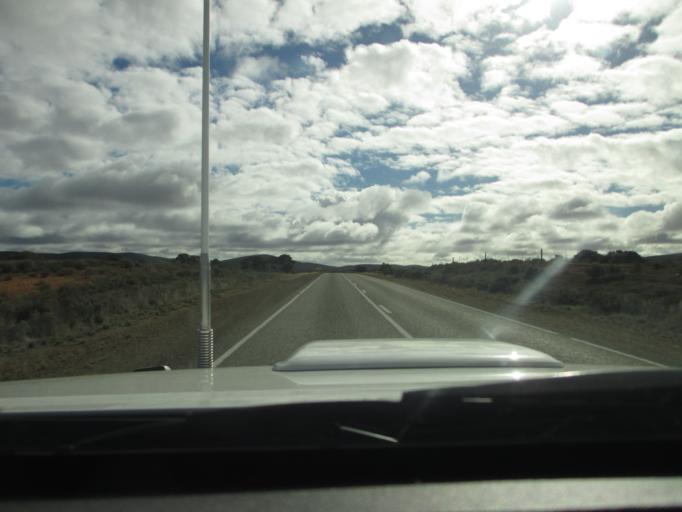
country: AU
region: South Australia
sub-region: Flinders Ranges
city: Quorn
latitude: -32.2337
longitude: 138.5140
